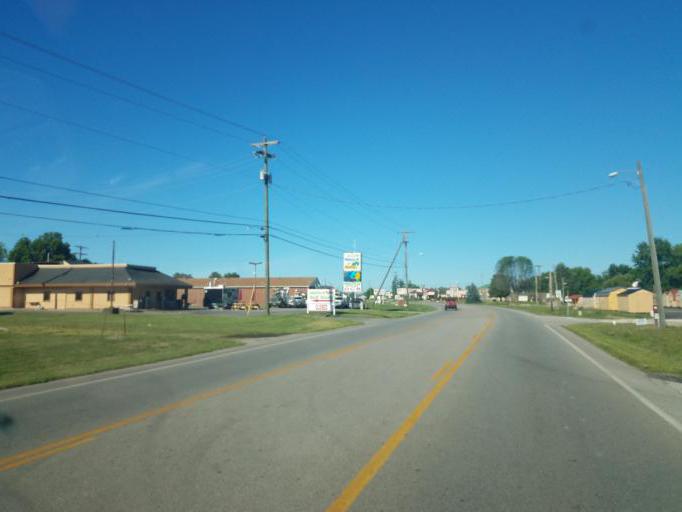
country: US
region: West Virginia
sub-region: Mason County
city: Point Pleasant
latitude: 38.8289
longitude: -82.1640
